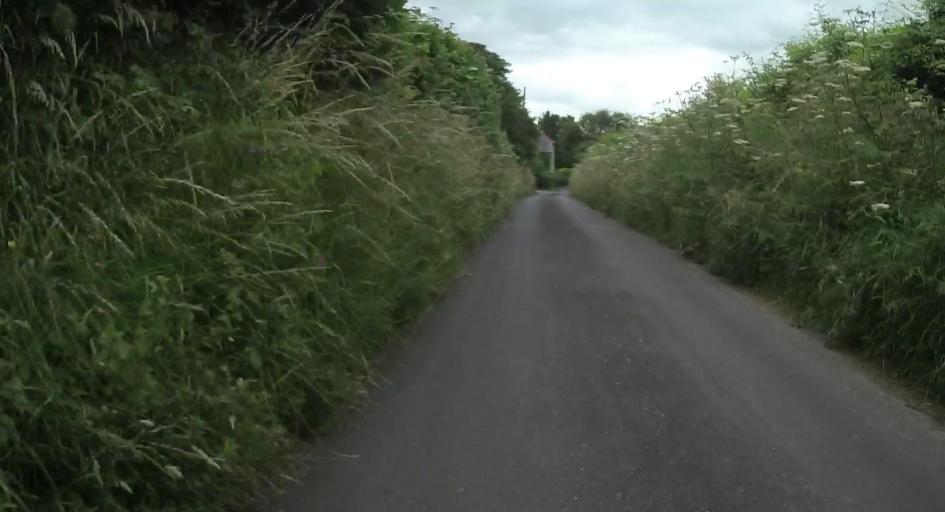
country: GB
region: England
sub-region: Hampshire
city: Kings Worthy
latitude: 51.0969
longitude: -1.2278
